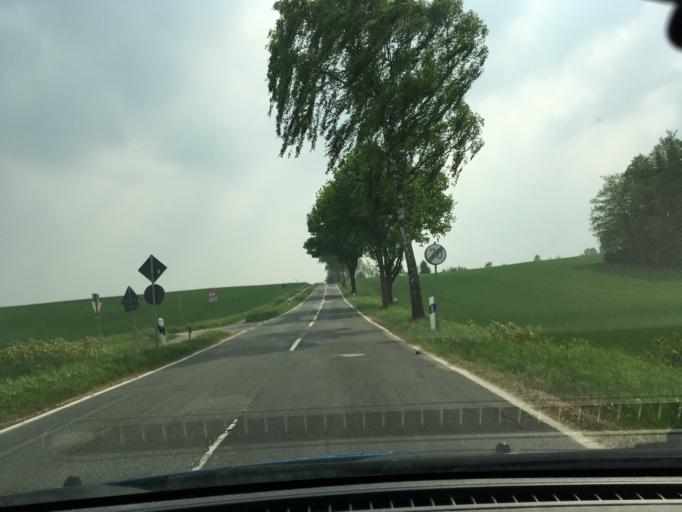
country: DE
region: Lower Saxony
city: Seevetal
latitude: 53.4170
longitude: 9.8951
